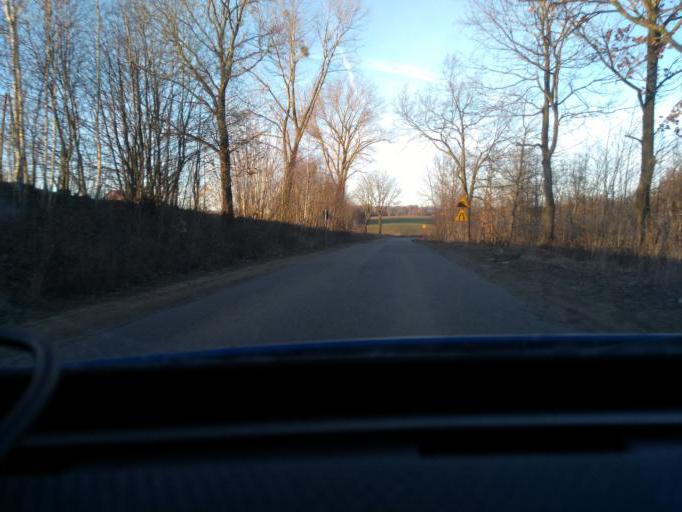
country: PL
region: Pomeranian Voivodeship
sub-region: Powiat kartuski
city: Przodkowo
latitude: 54.4017
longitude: 18.2892
